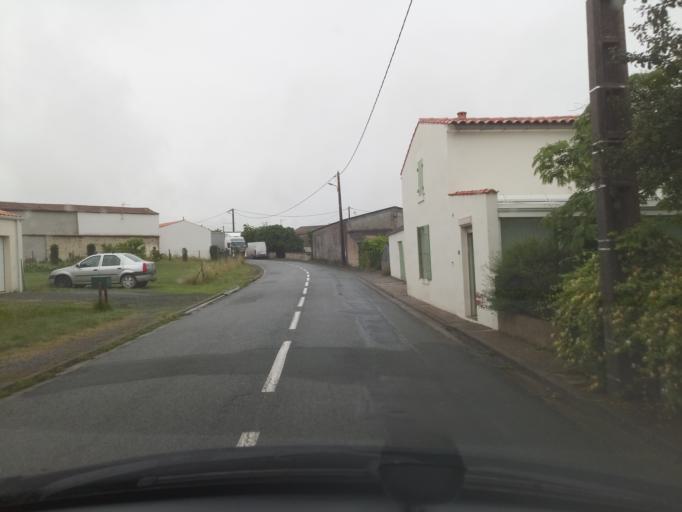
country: FR
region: Poitou-Charentes
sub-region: Departement de la Charente-Maritime
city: Andilly
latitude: 46.2312
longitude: -0.9955
